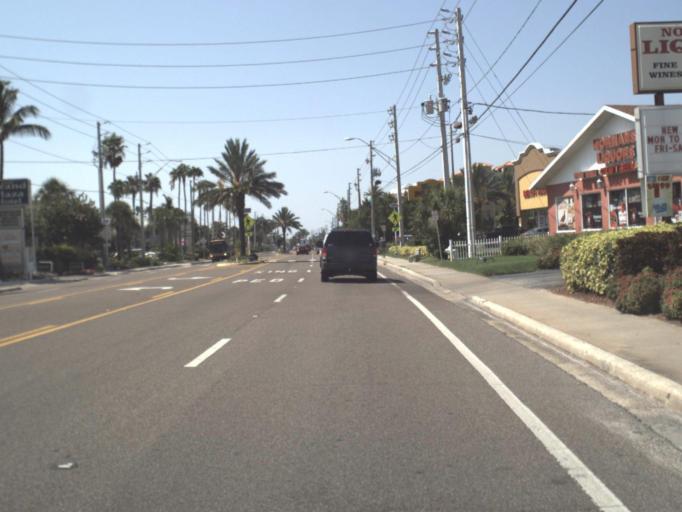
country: US
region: Florida
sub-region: Pinellas County
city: Saint Pete Beach
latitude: 27.7260
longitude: -82.7416
